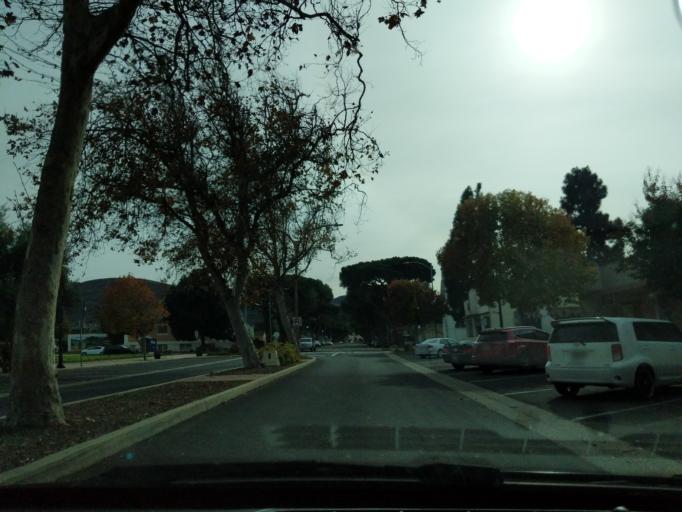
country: US
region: California
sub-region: Santa Barbara County
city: Lompoc
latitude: 34.6379
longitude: -120.4580
